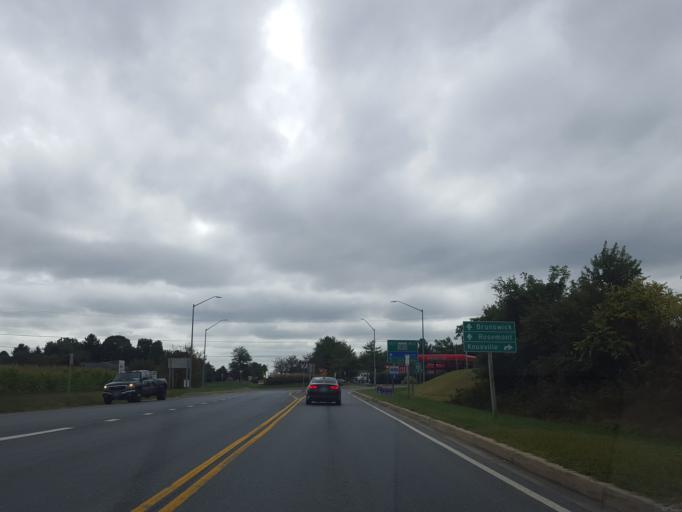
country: US
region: Maryland
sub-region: Frederick County
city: Brunswick
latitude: 39.3387
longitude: -77.6400
